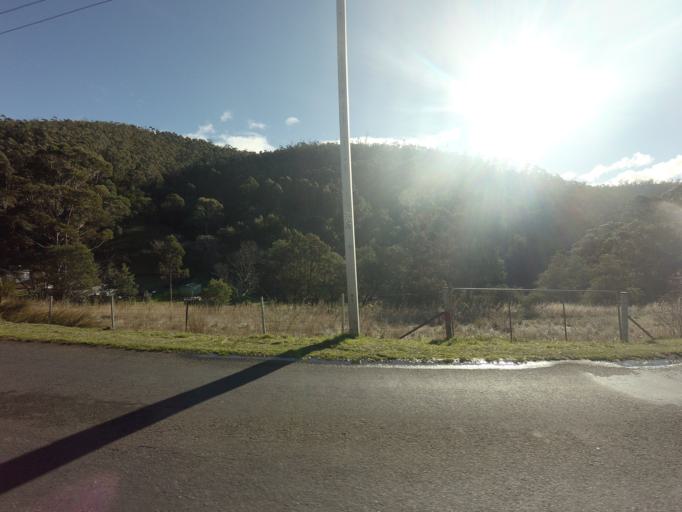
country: AU
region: Tasmania
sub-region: Glenorchy
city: Berriedale
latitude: -42.8180
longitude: 147.2223
